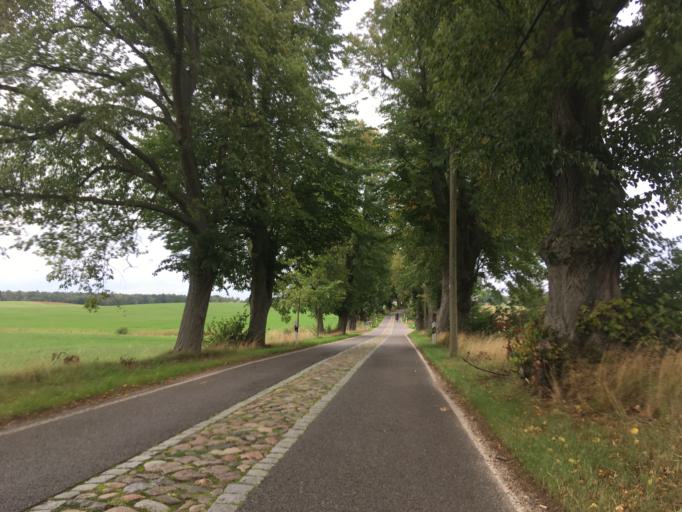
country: DE
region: Brandenburg
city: Joachimsthal
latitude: 53.0176
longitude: 13.7597
